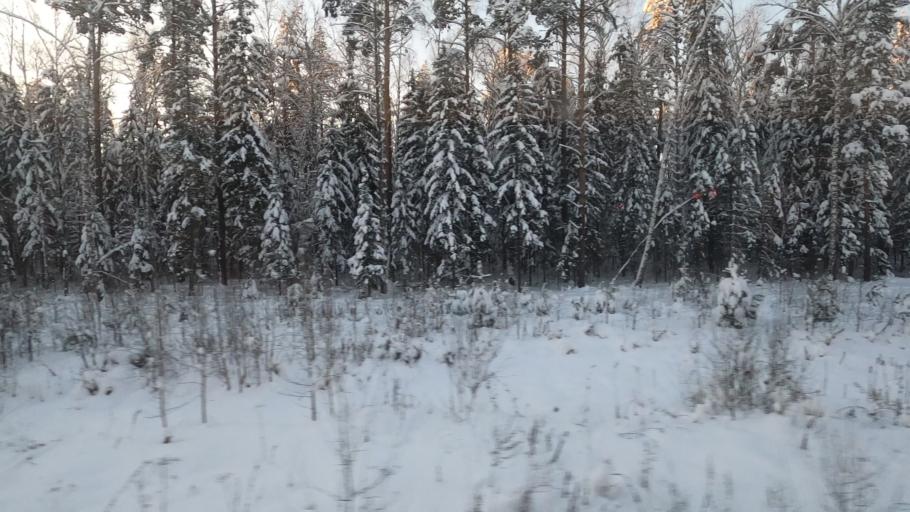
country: RU
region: Moskovskaya
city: Zhukovka
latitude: 56.5073
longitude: 37.5542
